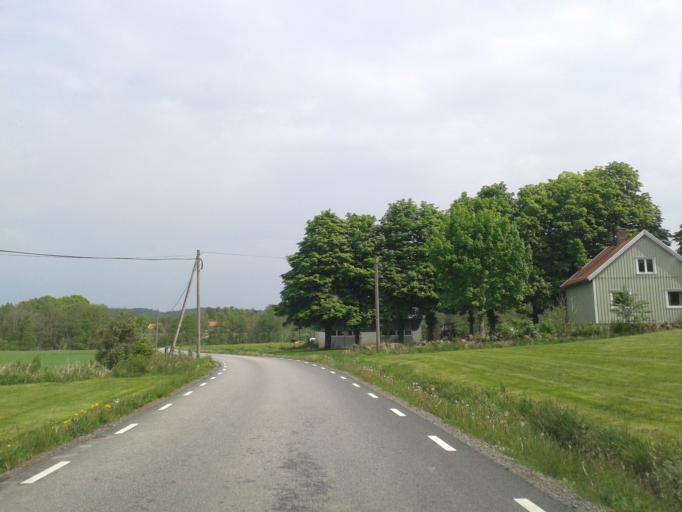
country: SE
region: Vaestra Goetaland
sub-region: Kungalvs Kommun
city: Kungalv
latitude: 57.9154
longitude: 11.9495
